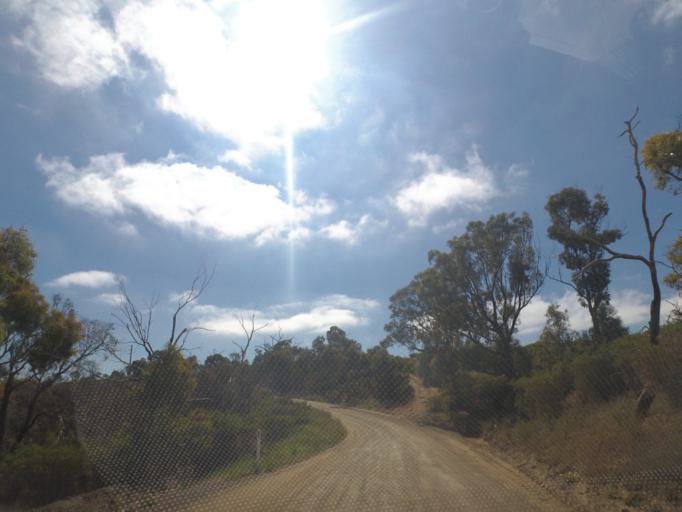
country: AU
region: Victoria
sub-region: Hume
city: Craigieburn
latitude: -37.4304
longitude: 144.9433
